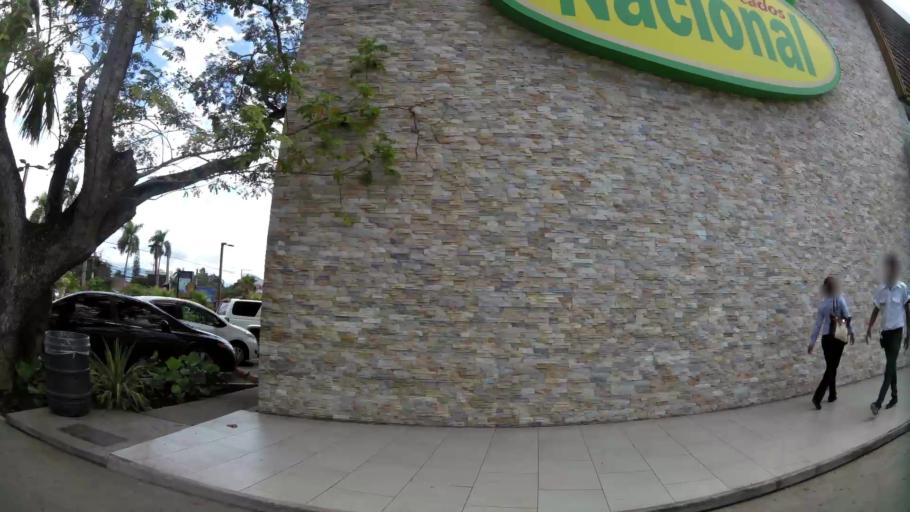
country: DO
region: Santiago
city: Santiago de los Caballeros
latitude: 19.4583
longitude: -70.6758
